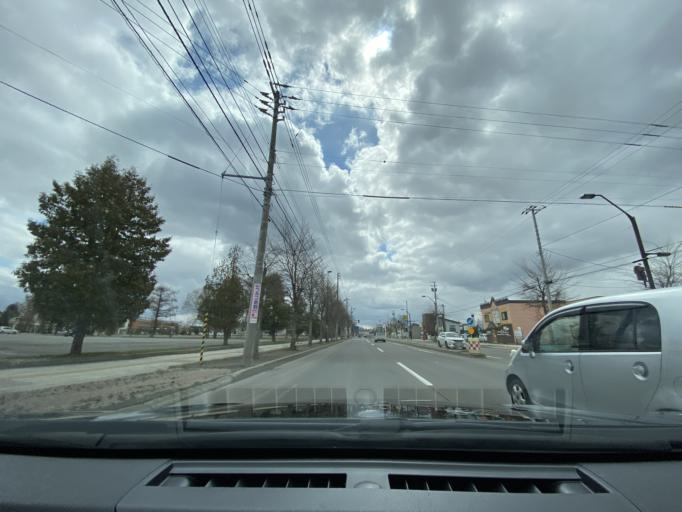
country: JP
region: Hokkaido
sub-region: Asahikawa-shi
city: Asahikawa
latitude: 43.7576
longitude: 142.3495
